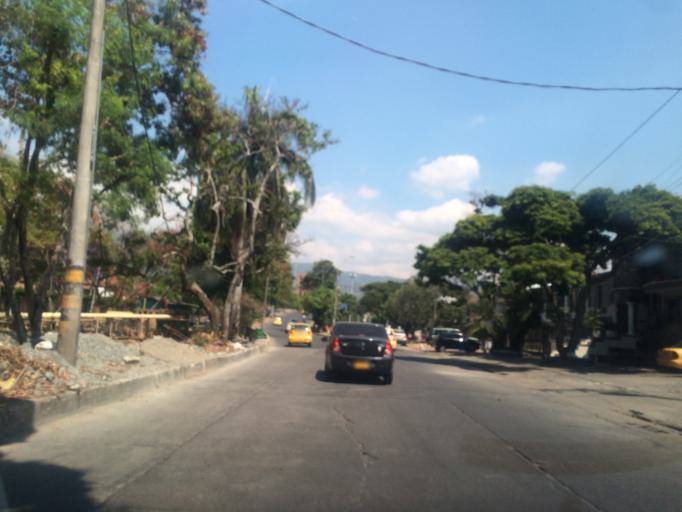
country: CO
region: Valle del Cauca
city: Cali
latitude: 3.4097
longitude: -76.5364
